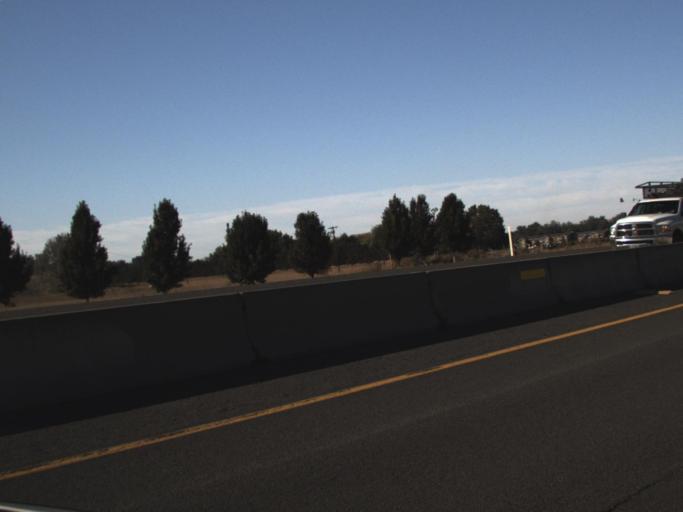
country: US
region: Washington
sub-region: Walla Walla County
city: College Place
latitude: 46.0079
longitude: -118.3901
